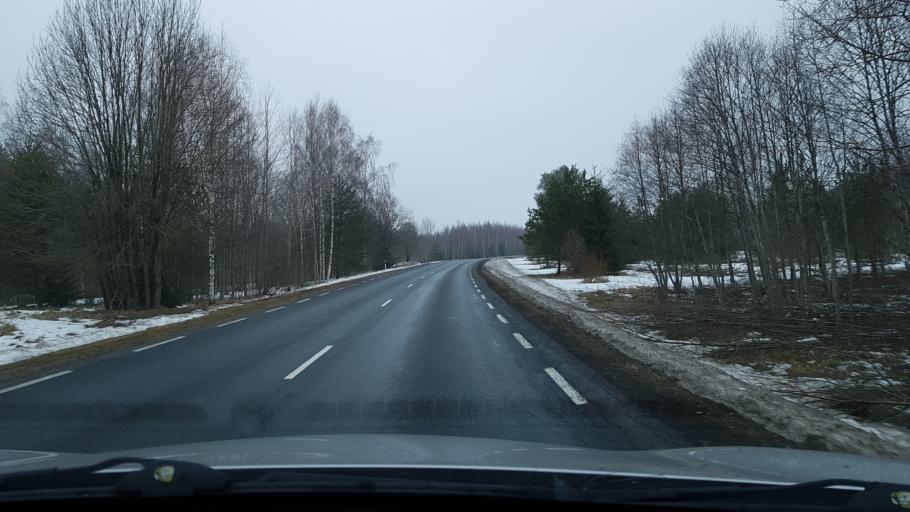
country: EE
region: Valgamaa
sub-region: Torva linn
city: Torva
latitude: 58.1202
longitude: 25.9934
